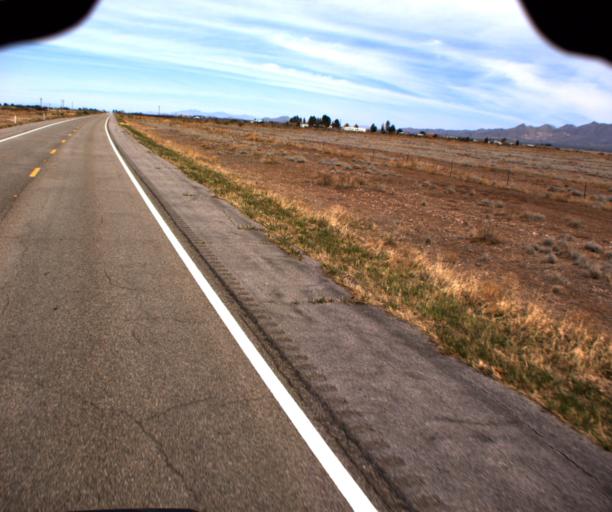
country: US
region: Arizona
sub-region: Cochise County
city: Pirtleville
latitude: 31.5649
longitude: -109.6676
